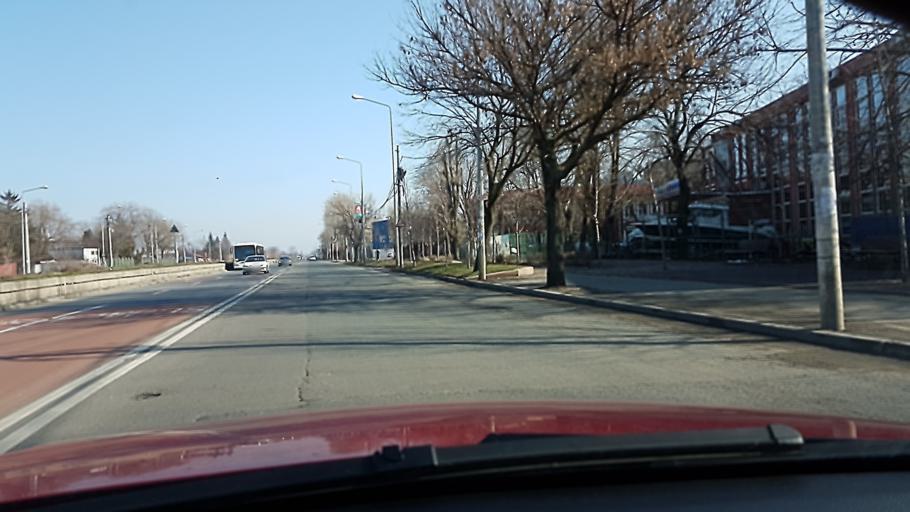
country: RO
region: Ilfov
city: Dobroesti
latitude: 44.4323
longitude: 26.1917
